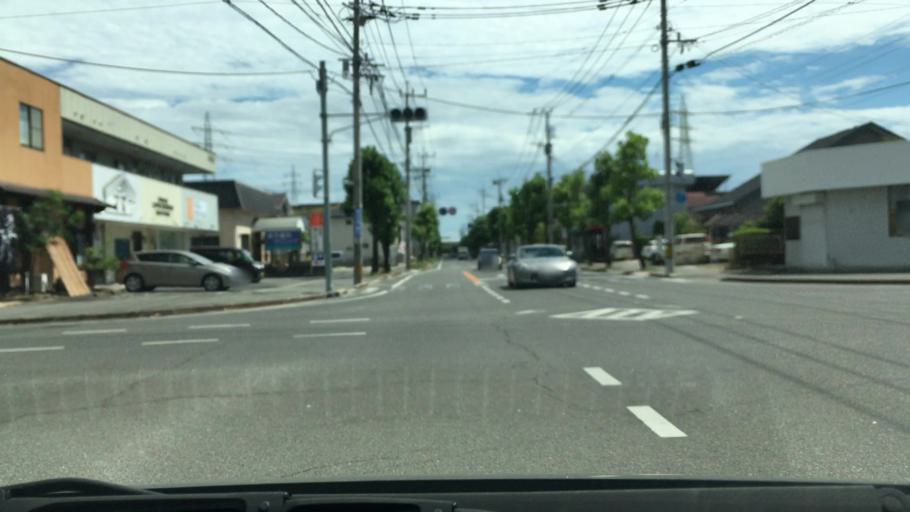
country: JP
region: Saga Prefecture
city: Saga-shi
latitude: 33.2699
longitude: 130.2869
